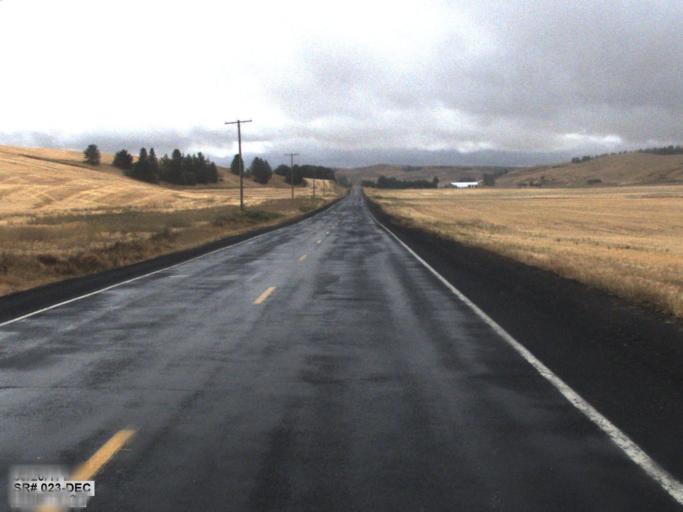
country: US
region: Washington
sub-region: Whitman County
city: Colfax
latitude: 47.0593
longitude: -117.5223
